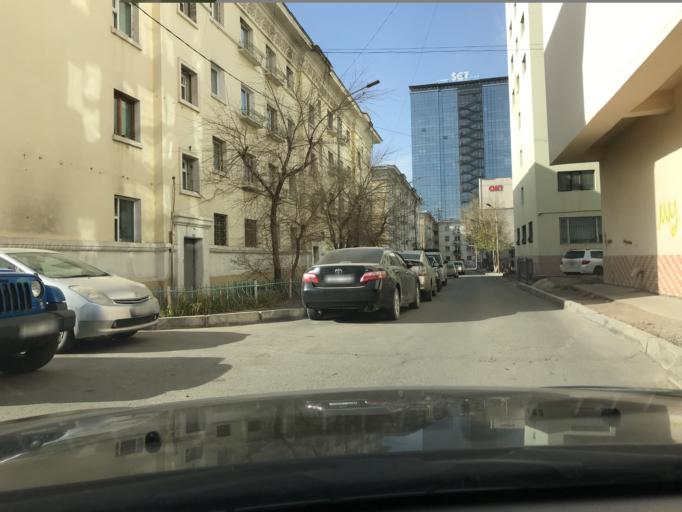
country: MN
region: Ulaanbaatar
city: Ulaanbaatar
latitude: 47.9165
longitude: 106.9051
